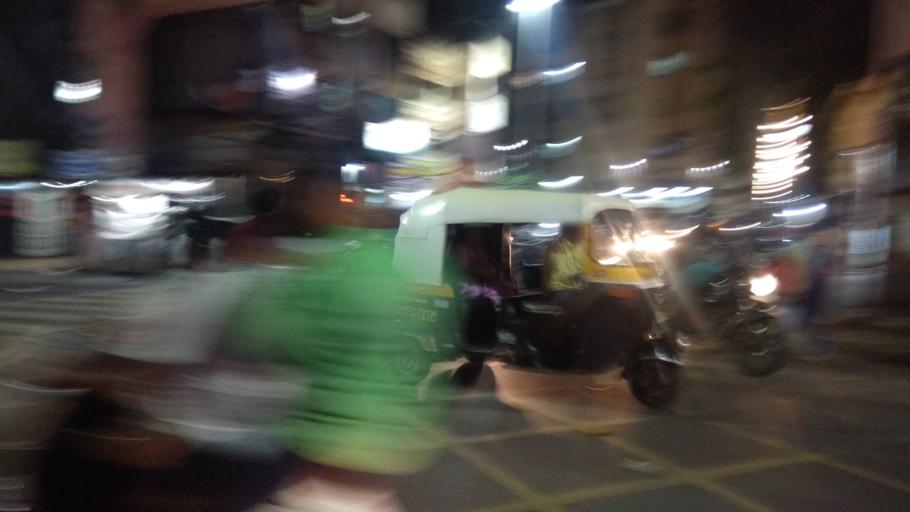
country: IN
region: Maharashtra
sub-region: Pune Division
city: Pune
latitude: 18.5187
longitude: 73.8573
